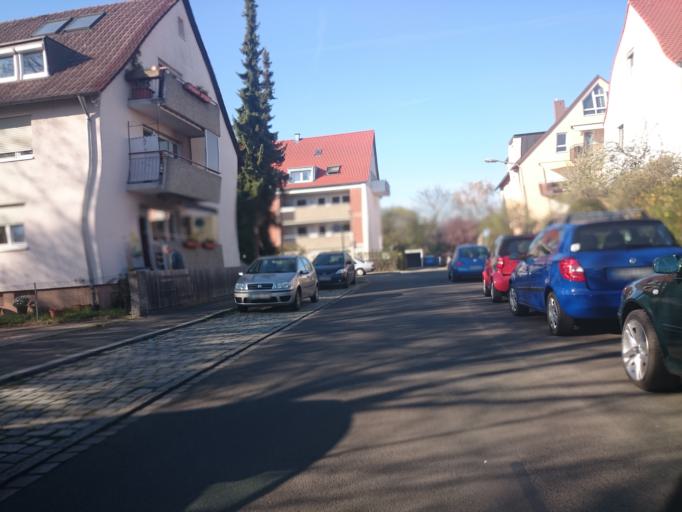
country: DE
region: Bavaria
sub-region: Regierungsbezirk Mittelfranken
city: Nuernberg
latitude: 49.4503
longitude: 11.1245
